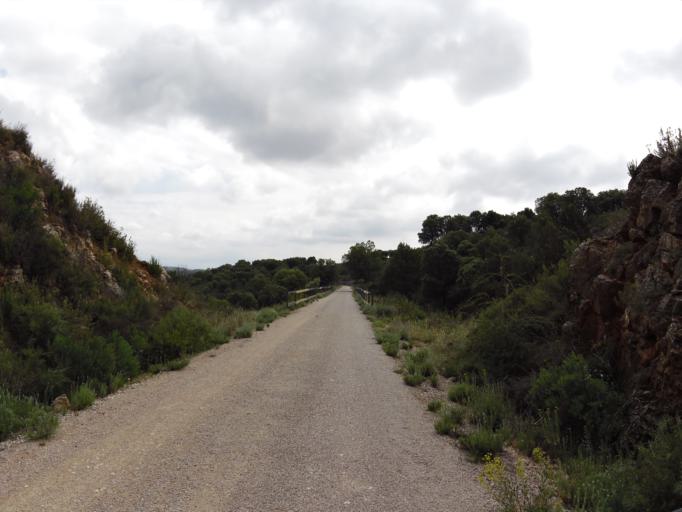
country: ES
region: Castille-La Mancha
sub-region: Provincia de Albacete
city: Robledo
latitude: 38.7710
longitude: -2.4184
